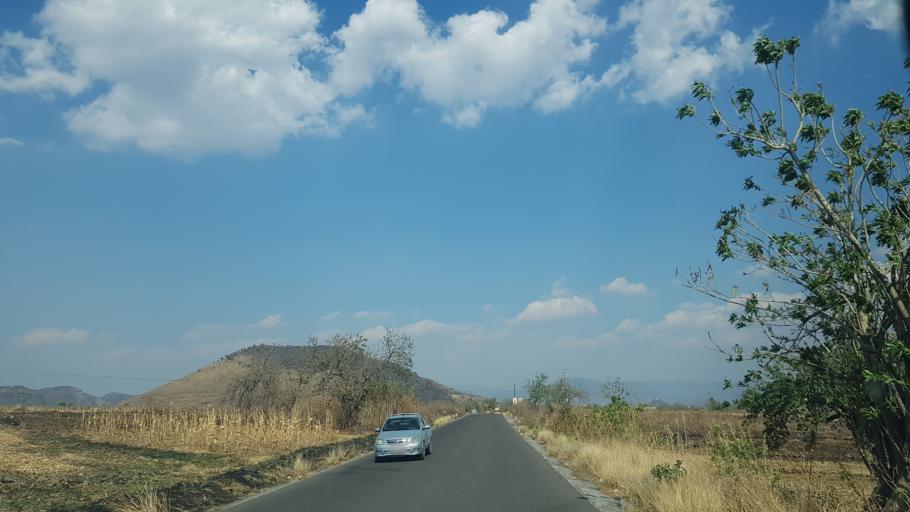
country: MX
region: Puebla
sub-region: Tianguismanalco
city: San Martin Tlapala
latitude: 18.9236
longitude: -98.4894
